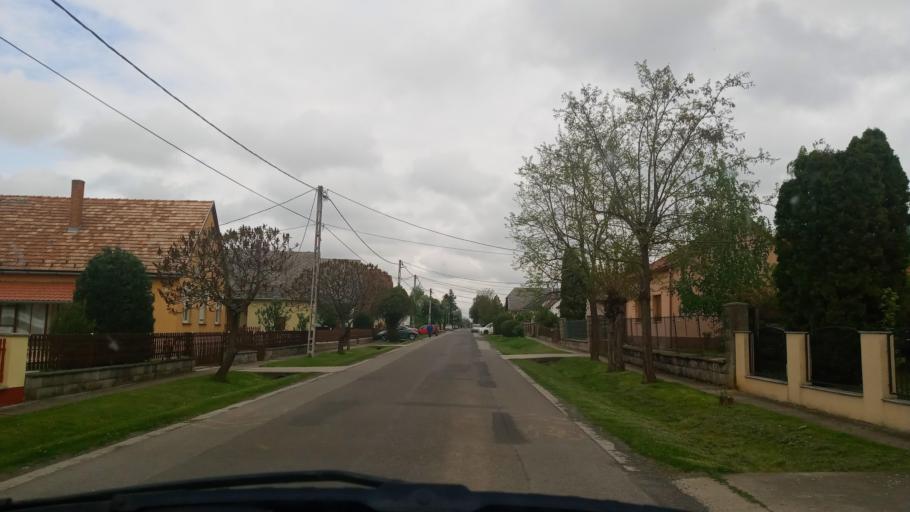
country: HU
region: Baranya
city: Kozarmisleny
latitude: 46.0009
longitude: 18.3752
